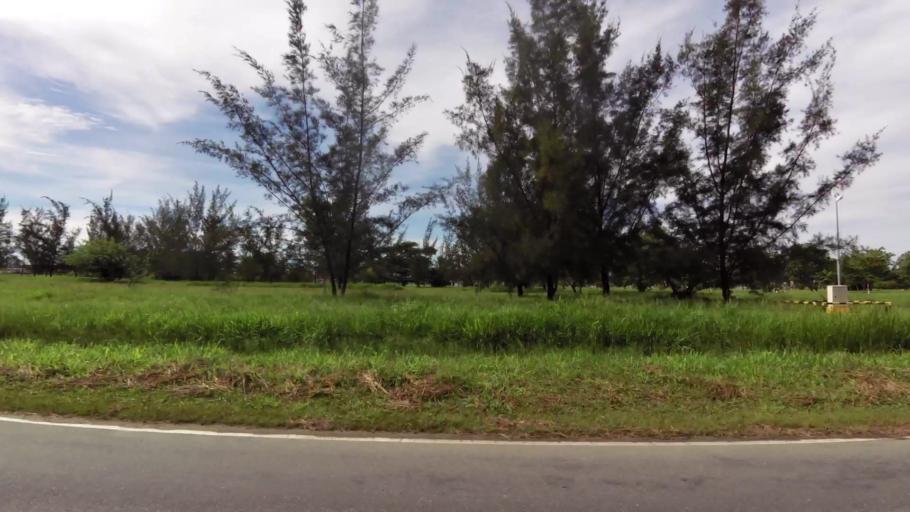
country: BN
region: Belait
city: Seria
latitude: 4.6194
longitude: 114.3289
